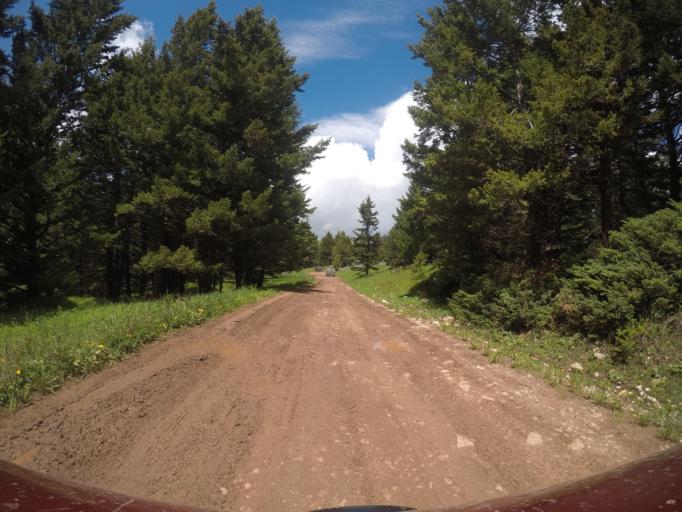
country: US
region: Wyoming
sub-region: Big Horn County
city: Lovell
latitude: 45.1743
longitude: -108.4340
